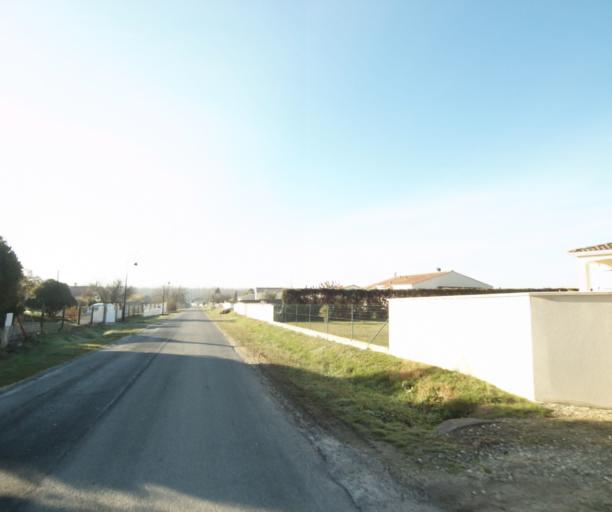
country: FR
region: Poitou-Charentes
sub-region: Departement de la Charente-Maritime
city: Cherac
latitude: 45.6899
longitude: -0.4504
